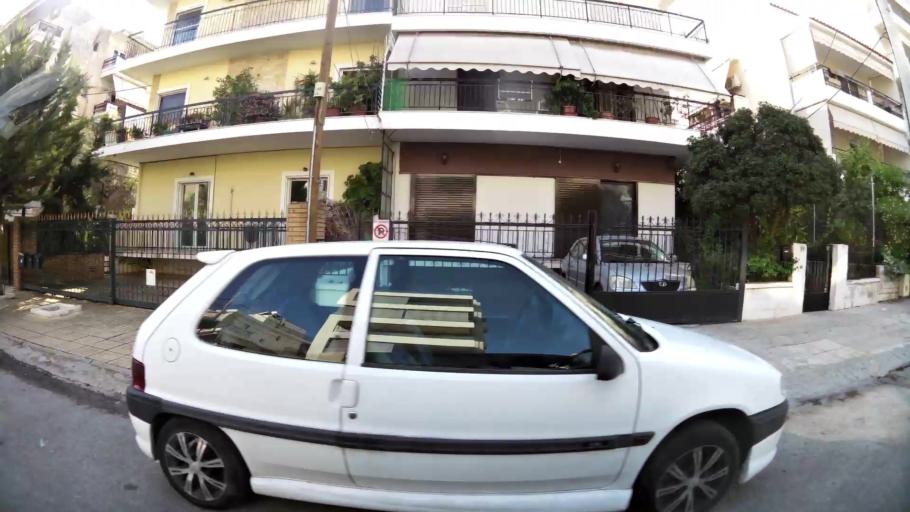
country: GR
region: Attica
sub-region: Nomarchia Athinas
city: Argyroupoli
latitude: 37.9022
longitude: 23.7536
